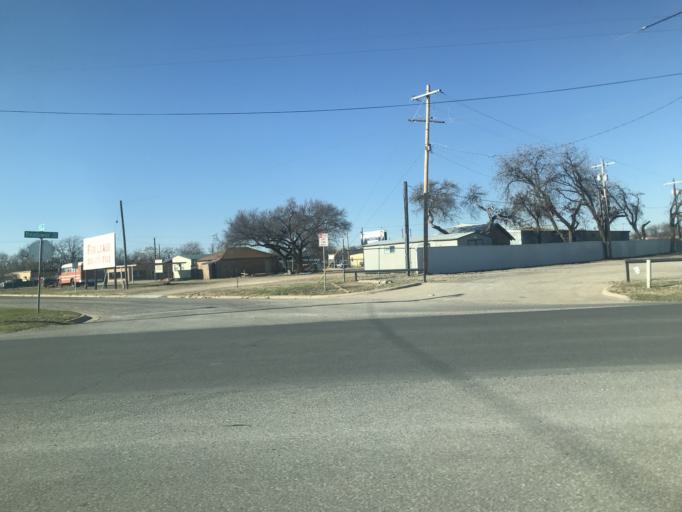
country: US
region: Texas
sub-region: Taylor County
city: Abilene
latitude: 32.4210
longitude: -99.7376
